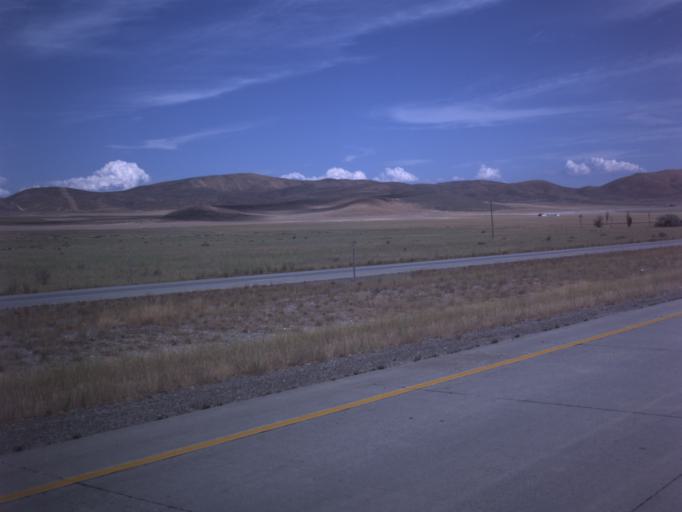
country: US
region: Utah
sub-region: Box Elder County
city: Garland
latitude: 41.8661
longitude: -112.4601
